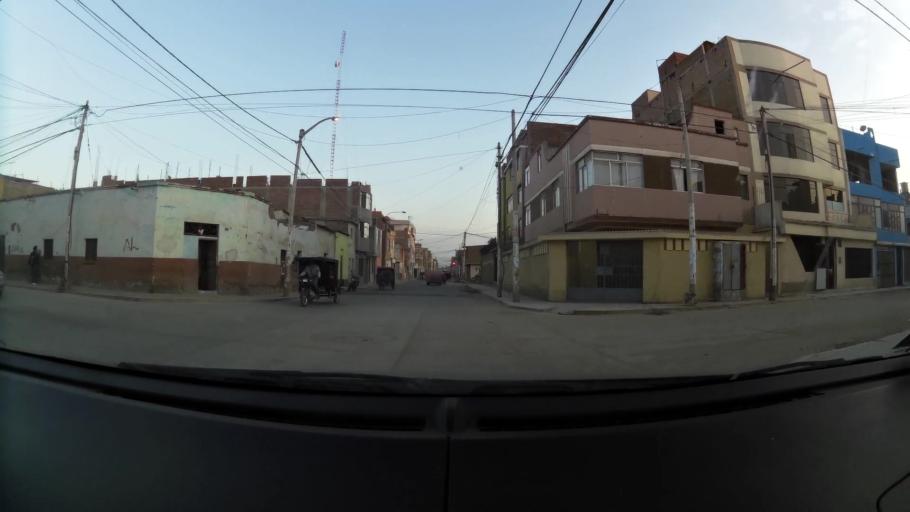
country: PE
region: Lambayeque
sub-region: Provincia de Chiclayo
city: Santa Rosa
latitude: -6.7662
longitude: -79.8318
